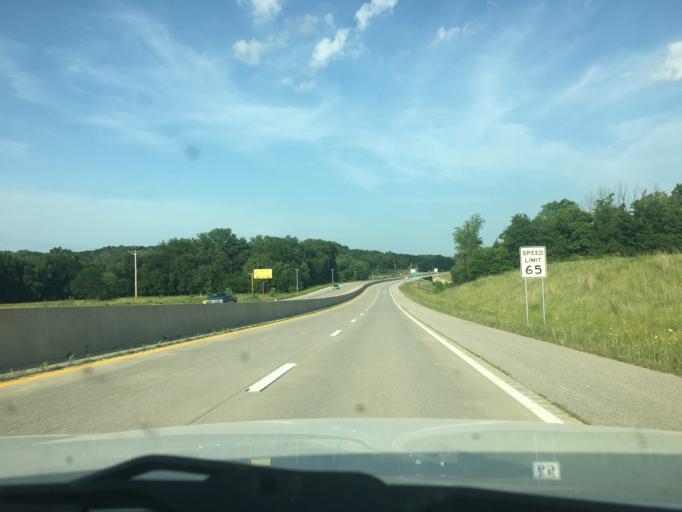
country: US
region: Missouri
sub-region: Osage County
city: Linn
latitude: 38.4940
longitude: -91.9920
